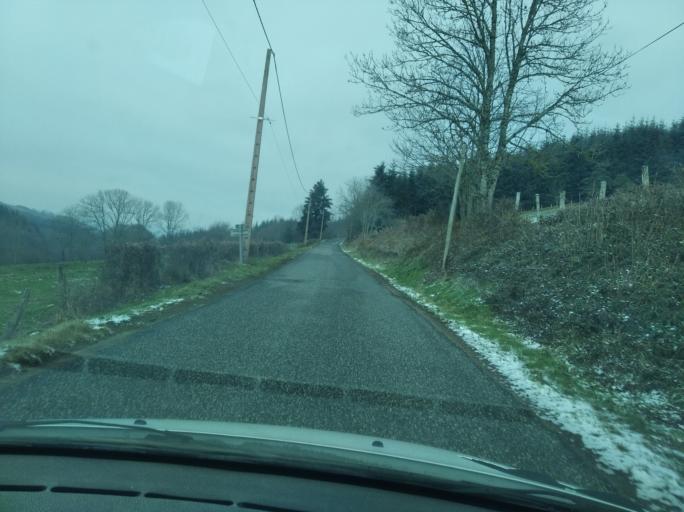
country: FR
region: Rhone-Alpes
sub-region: Departement de la Loire
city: La Pacaudiere
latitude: 46.1187
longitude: 3.7969
